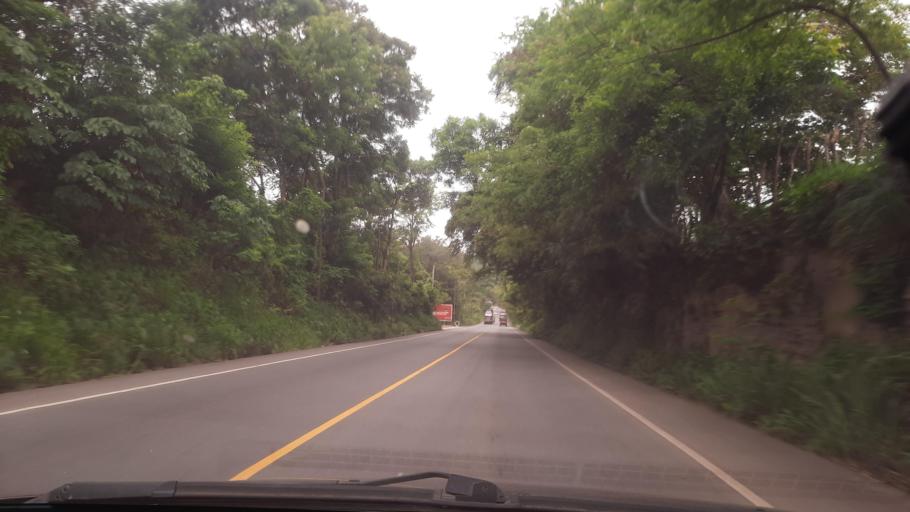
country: GT
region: Zacapa
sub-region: Municipio de Zacapa
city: Gualan
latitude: 15.1702
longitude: -89.3070
